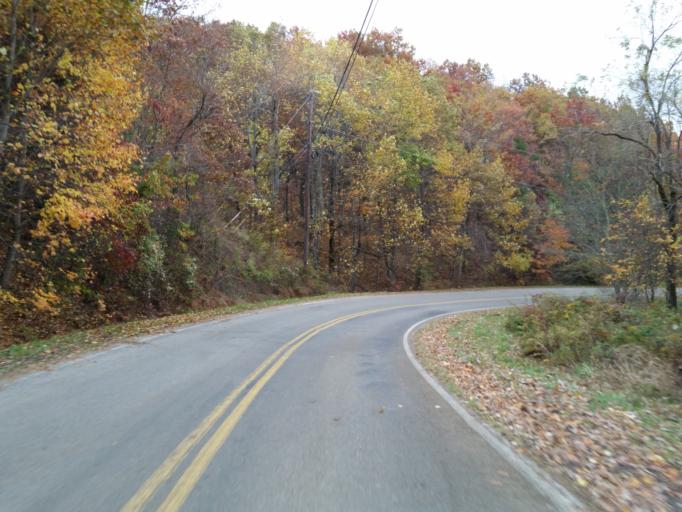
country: US
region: Georgia
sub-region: Pickens County
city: Jasper
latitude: 34.5568
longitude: -84.3481
